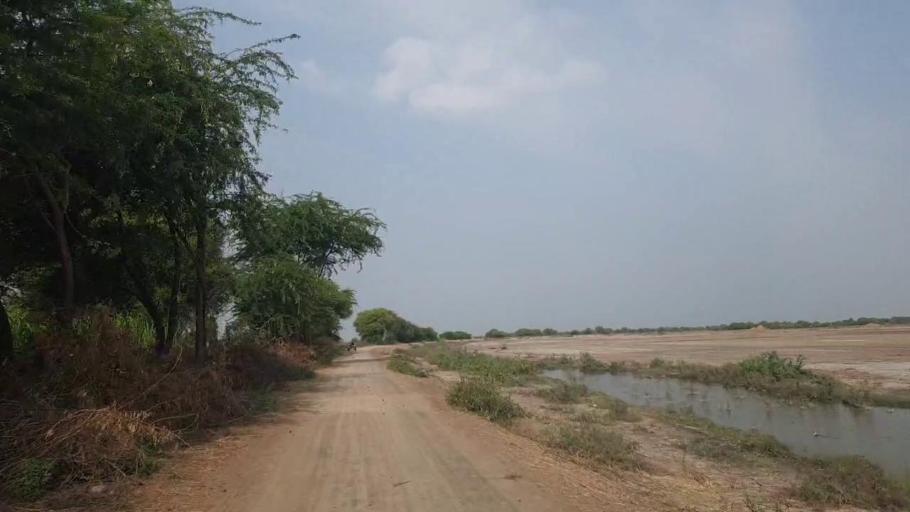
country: PK
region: Sindh
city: Badin
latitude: 24.5521
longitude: 68.7310
